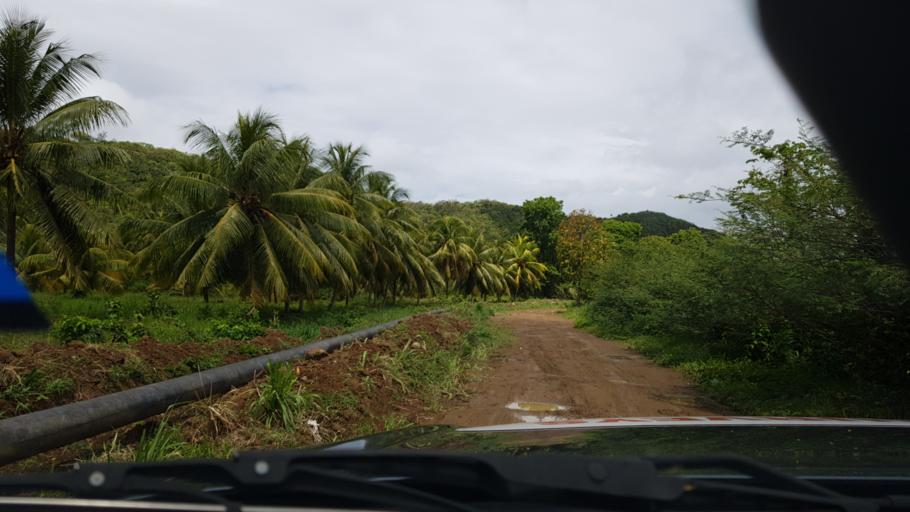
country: LC
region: Anse-la-Raye
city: Anse La Raye
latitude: 13.9536
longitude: -61.0295
